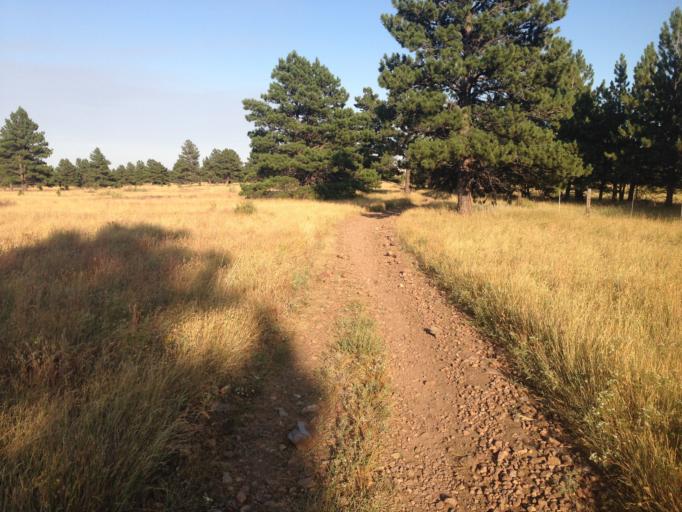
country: US
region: Colorado
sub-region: Boulder County
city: Superior
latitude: 39.9141
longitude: -105.2543
